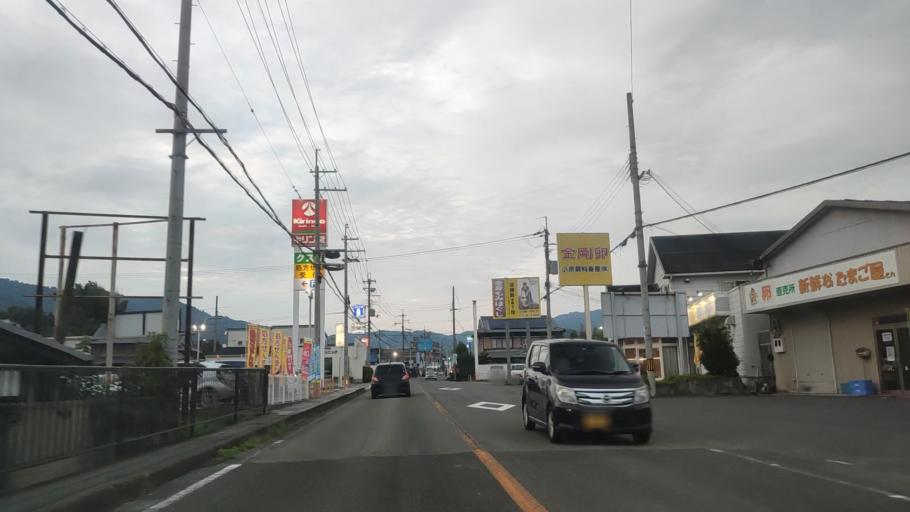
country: JP
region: Wakayama
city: Hashimoto
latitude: 34.3361
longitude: 135.6058
